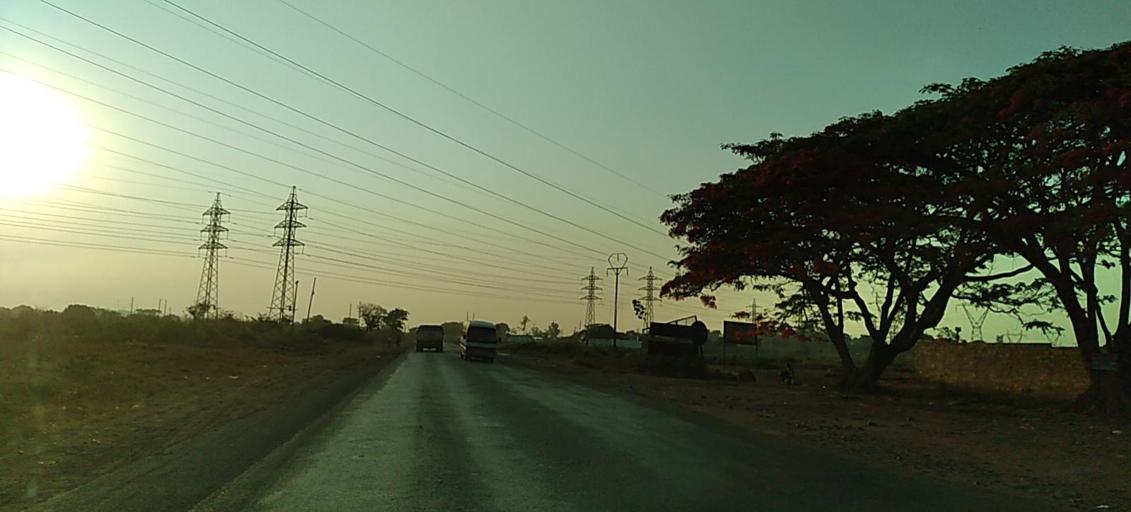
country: ZM
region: Copperbelt
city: Ndola
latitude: -13.0206
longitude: 28.6698
